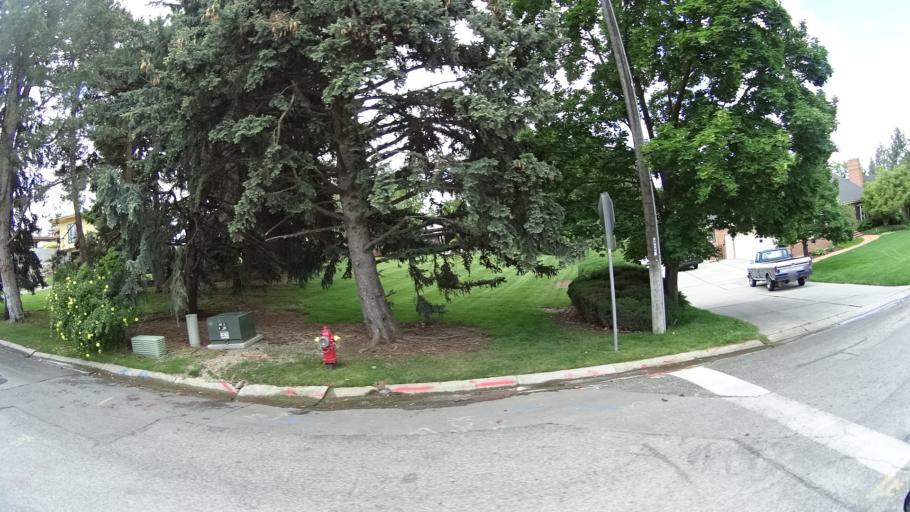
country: US
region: Idaho
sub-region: Ada County
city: Boise
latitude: 43.6459
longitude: -116.1904
